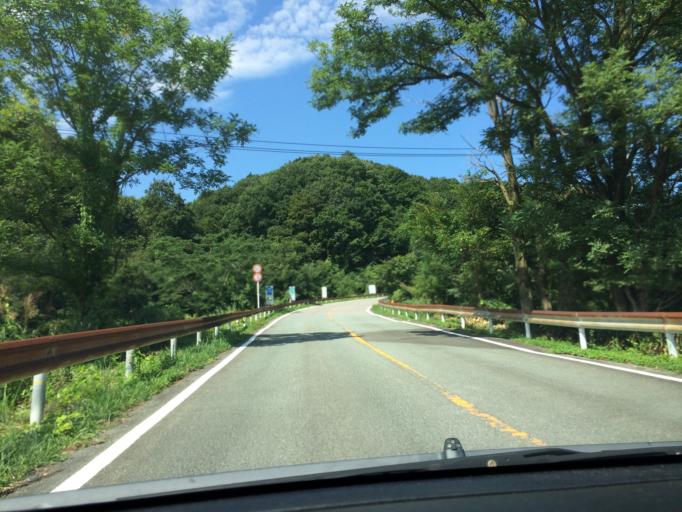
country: JP
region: Tottori
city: Kurayoshi
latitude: 35.3014
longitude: 133.6249
